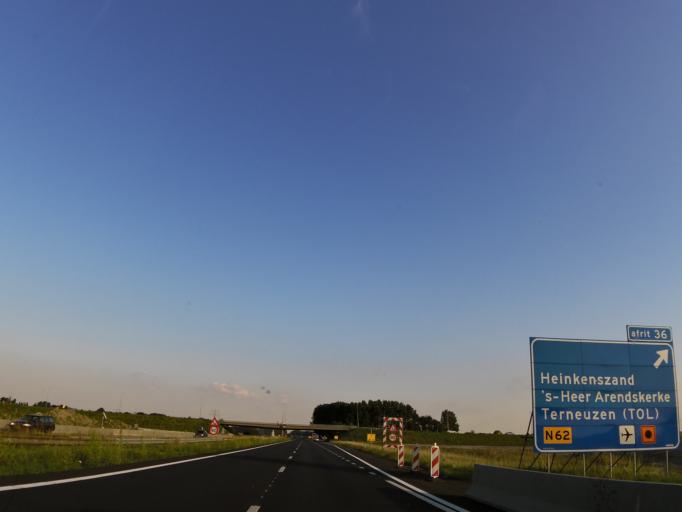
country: NL
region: Zeeland
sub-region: Gemeente Borsele
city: Borssele
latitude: 51.4897
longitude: 3.7927
